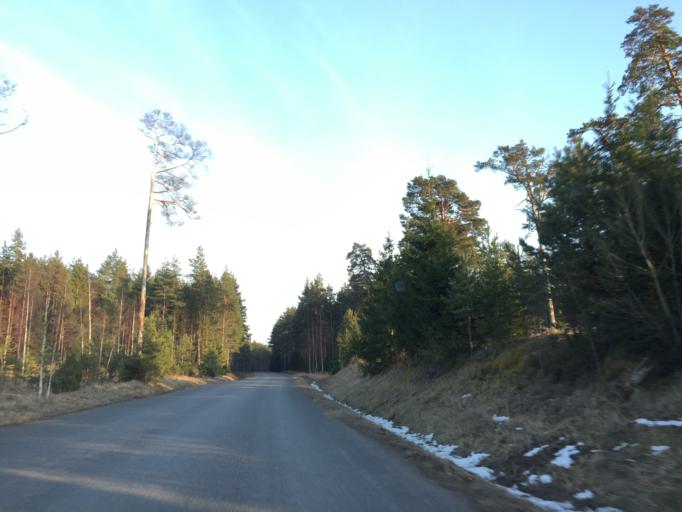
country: EE
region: Laeaene
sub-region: Lihula vald
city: Lihula
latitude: 58.4706
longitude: 23.7135
